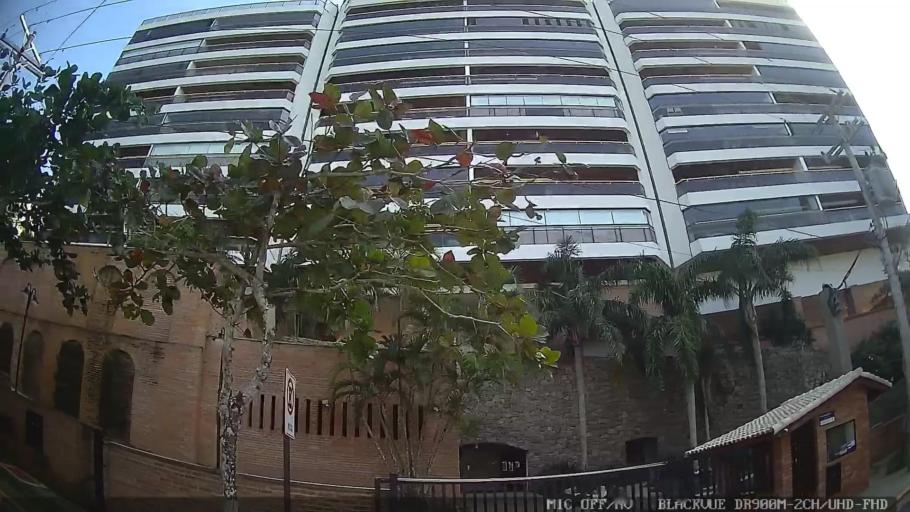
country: BR
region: Sao Paulo
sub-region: Guaruja
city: Guaruja
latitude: -23.9817
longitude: -46.1887
